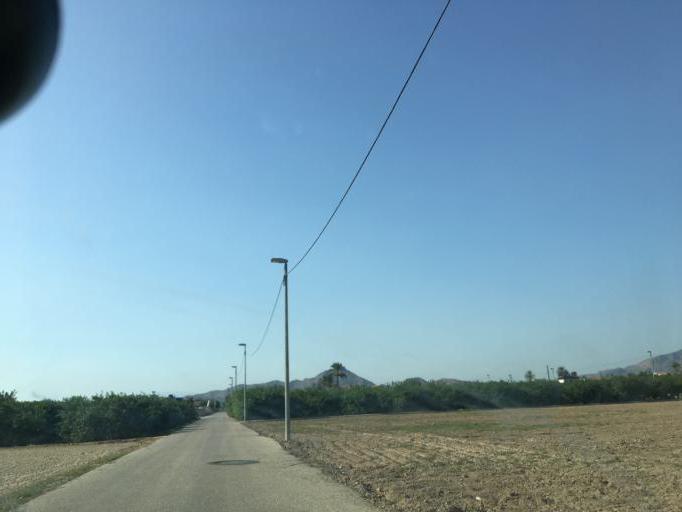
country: ES
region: Murcia
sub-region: Murcia
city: Santomera
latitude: 38.0234
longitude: -1.0524
